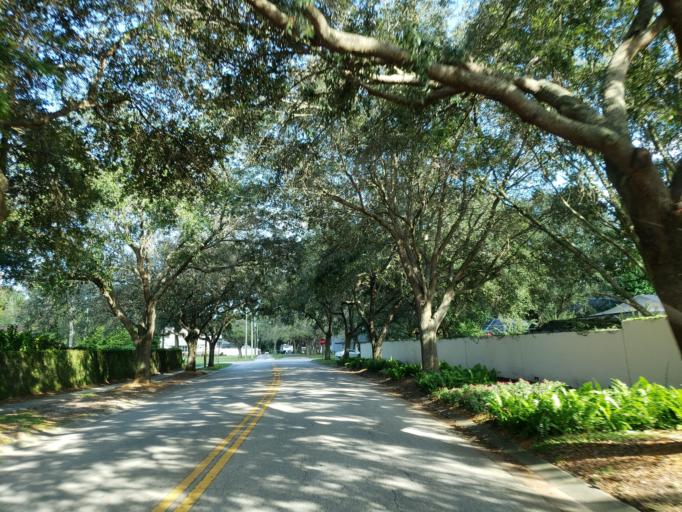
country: US
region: Florida
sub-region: Hillsborough County
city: Bloomingdale
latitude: 27.8735
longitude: -82.2452
